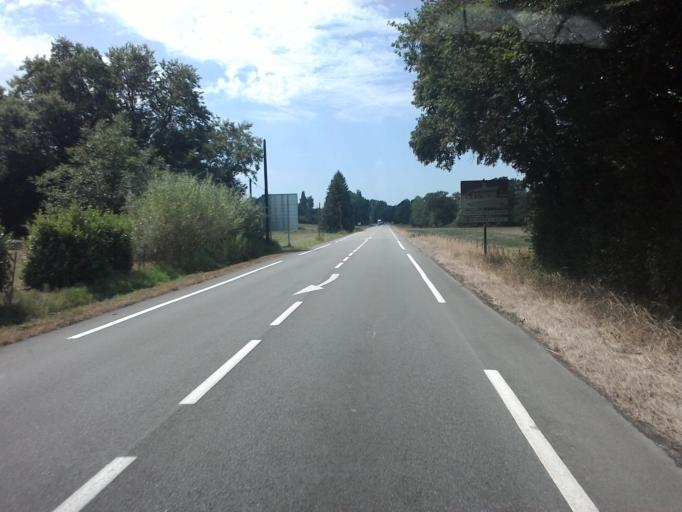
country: FR
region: Rhone-Alpes
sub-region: Departement de l'Ain
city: Saint-Etienne-du-Bois
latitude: 46.3283
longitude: 5.3123
